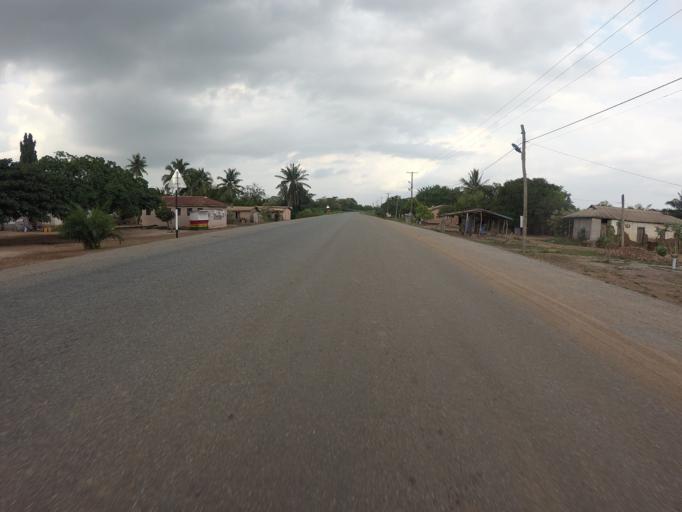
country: GH
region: Volta
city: Ho
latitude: 6.4269
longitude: 0.5125
